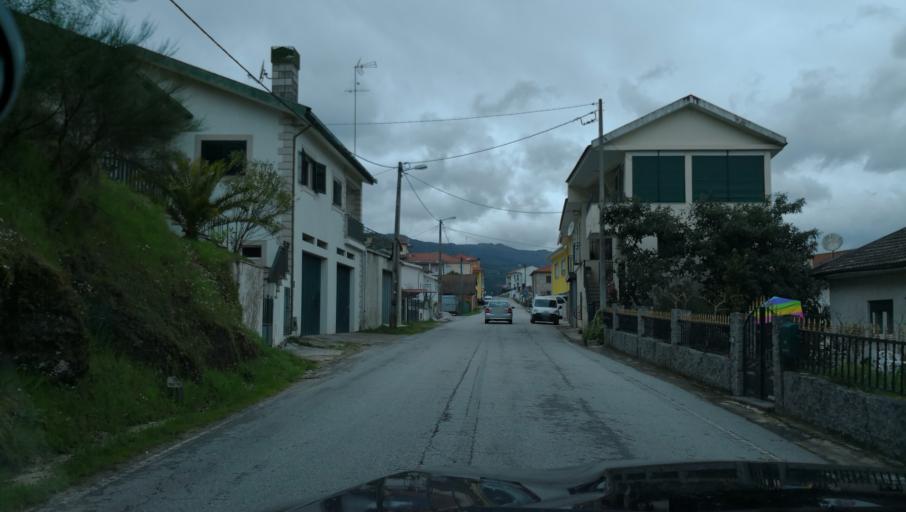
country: PT
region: Vila Real
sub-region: Vila Real
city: Vila Real
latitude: 41.2770
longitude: -7.7778
